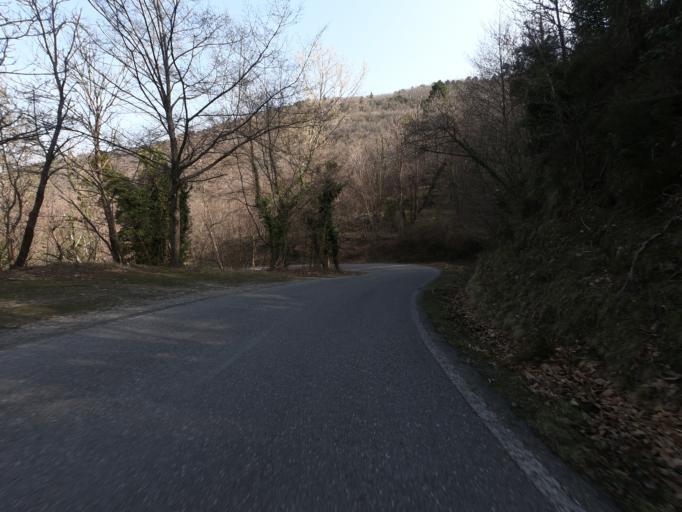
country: IT
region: Liguria
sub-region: Provincia di Savona
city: Zuccarello
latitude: 44.1214
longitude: 8.1394
